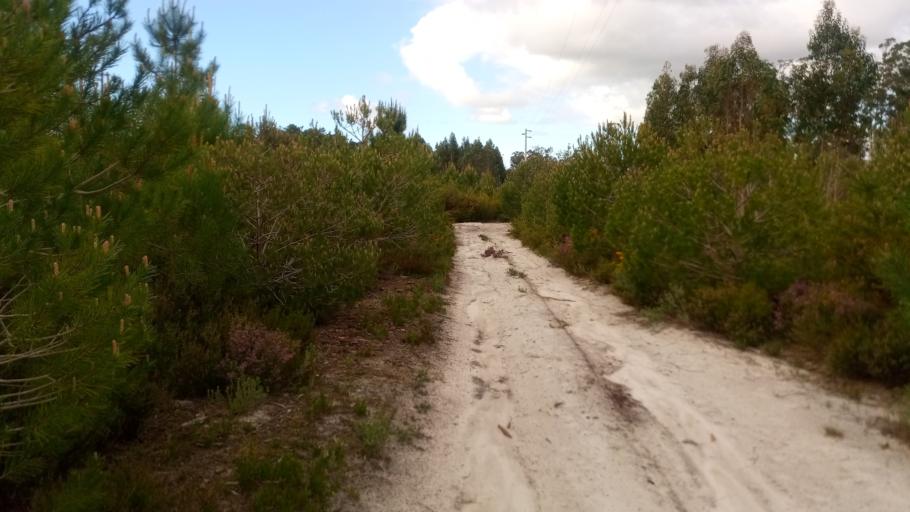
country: PT
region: Leiria
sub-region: Caldas da Rainha
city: Caldas da Rainha
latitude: 39.4427
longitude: -9.1668
